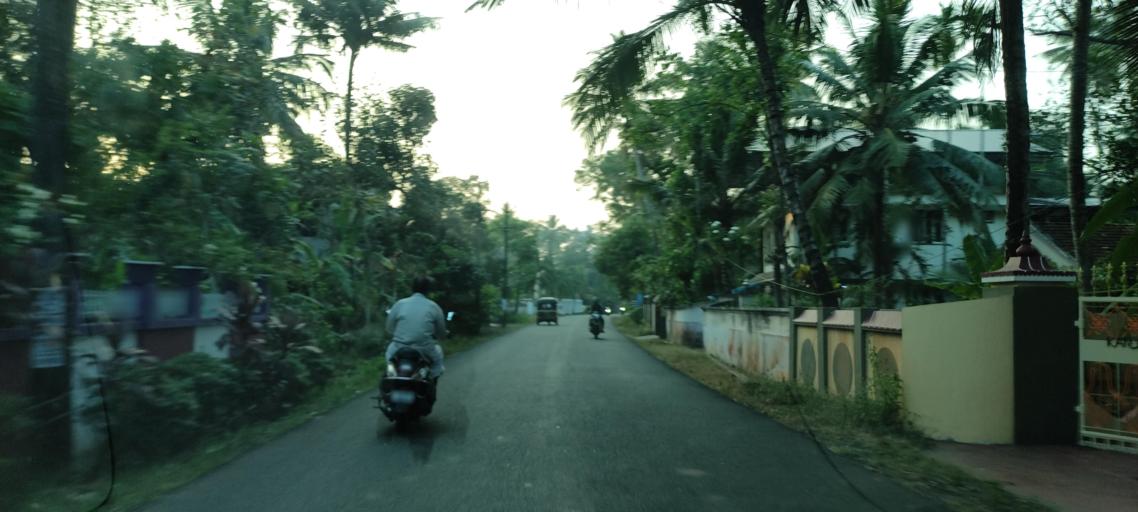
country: IN
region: Kerala
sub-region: Alappuzha
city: Kattanam
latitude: 9.1349
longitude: 76.5388
